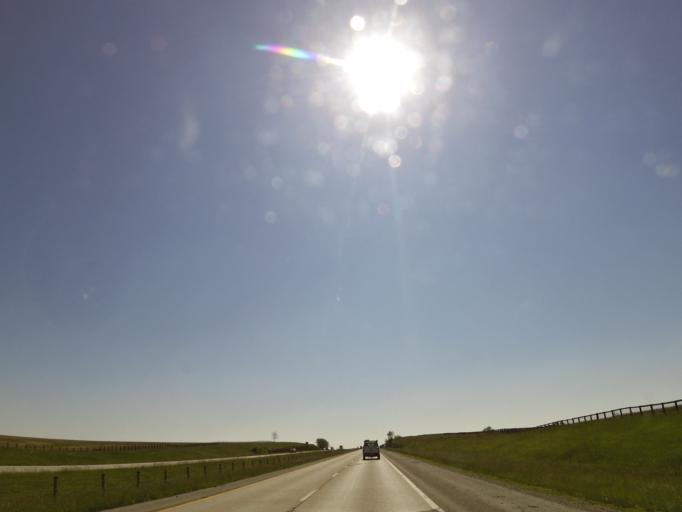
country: US
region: Kentucky
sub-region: Woodford County
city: Midway
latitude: 38.1613
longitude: -84.7066
